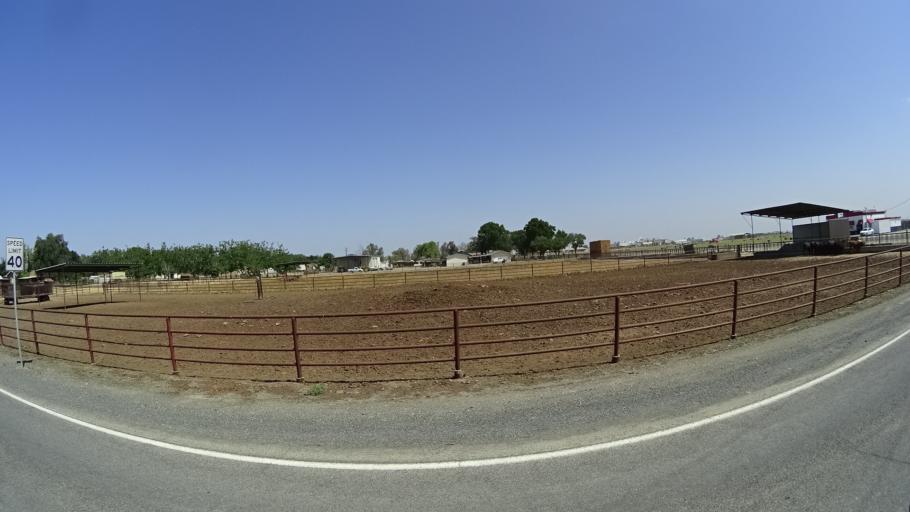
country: US
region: California
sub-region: Kings County
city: Home Garden
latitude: 36.3135
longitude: -119.6197
